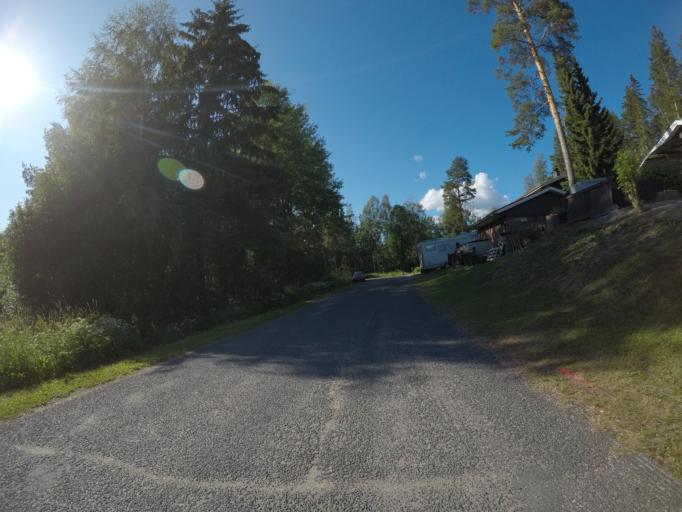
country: FI
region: Haeme
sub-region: Haemeenlinna
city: Haemeenlinna
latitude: 61.0195
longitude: 24.4971
